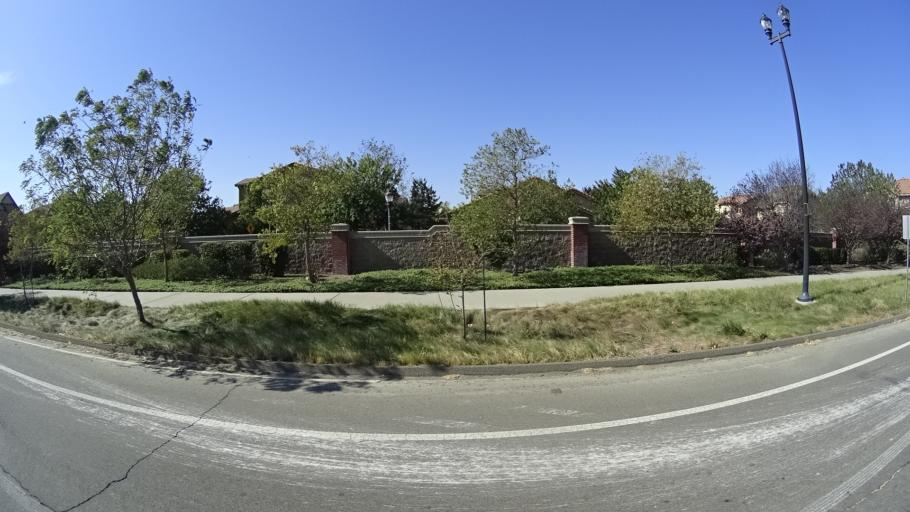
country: US
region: California
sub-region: Yolo County
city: Woodland
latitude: 38.6540
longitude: -121.7289
